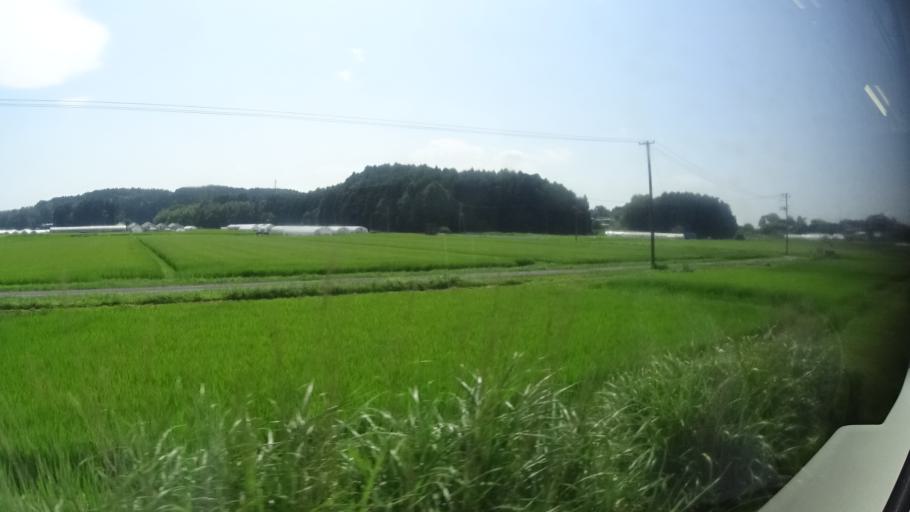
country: JP
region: Miyagi
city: Wakuya
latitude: 38.5250
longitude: 141.1591
